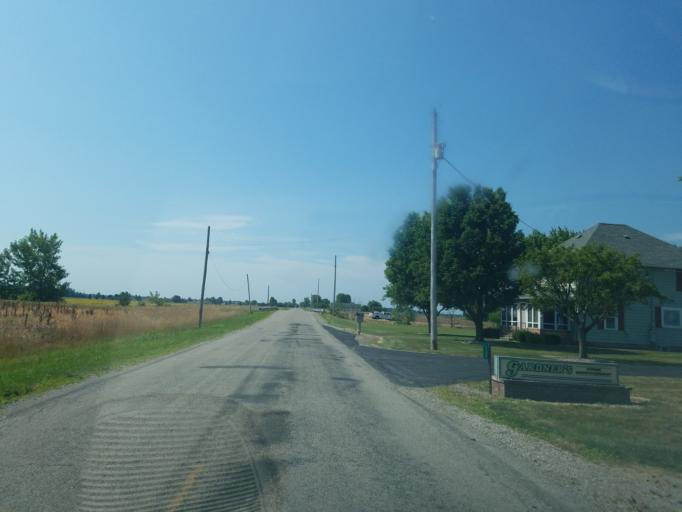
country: US
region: Ohio
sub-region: Van Wert County
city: Van Wert
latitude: 40.9126
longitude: -84.6295
